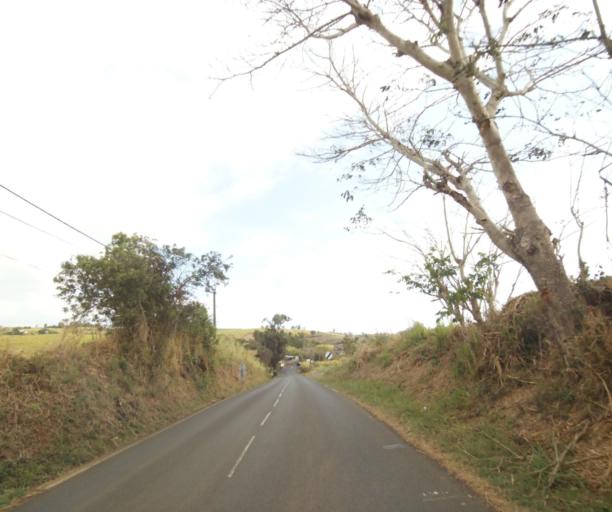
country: RE
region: Reunion
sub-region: Reunion
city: Trois-Bassins
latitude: -21.0700
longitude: 55.2779
